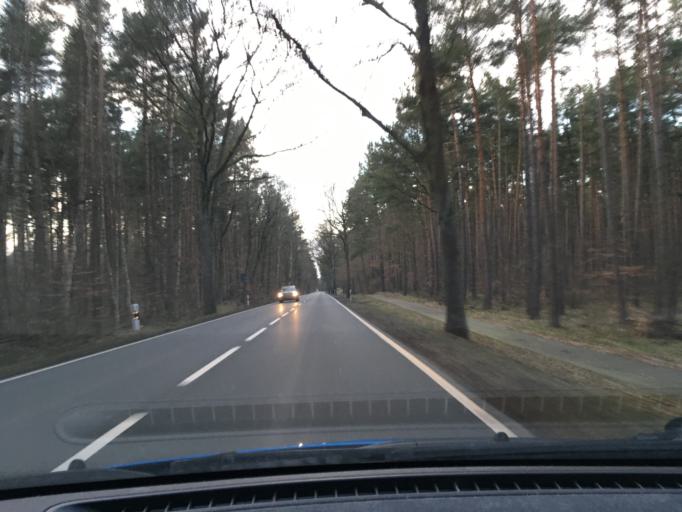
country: DE
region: Lower Saxony
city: Karwitz
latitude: 53.1188
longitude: 10.9896
